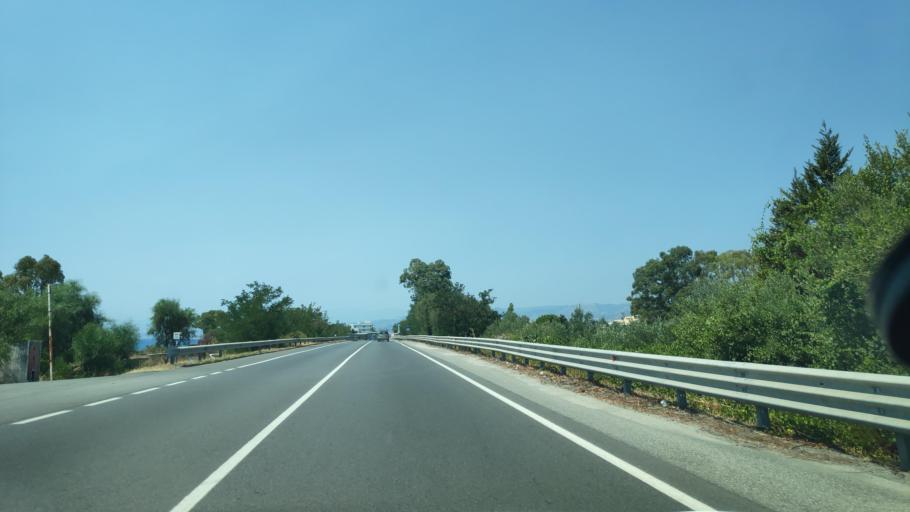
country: IT
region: Calabria
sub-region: Provincia di Reggio Calabria
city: Roccella Ionica
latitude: 38.3092
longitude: 16.3680
